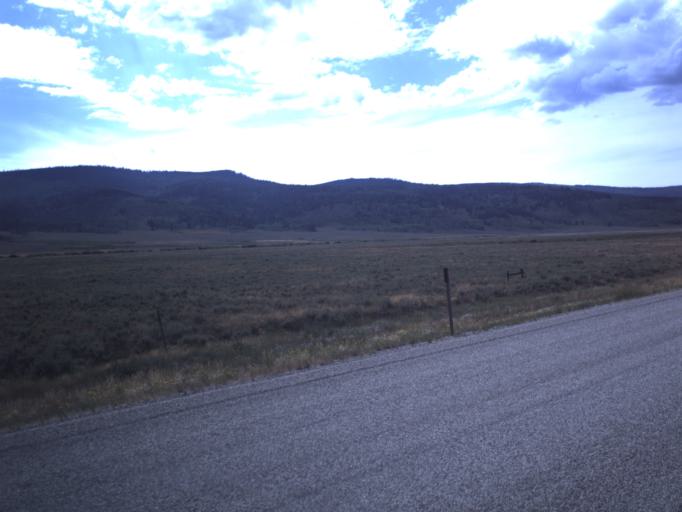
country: US
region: Utah
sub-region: Wasatch County
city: Heber
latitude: 40.2567
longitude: -111.2013
